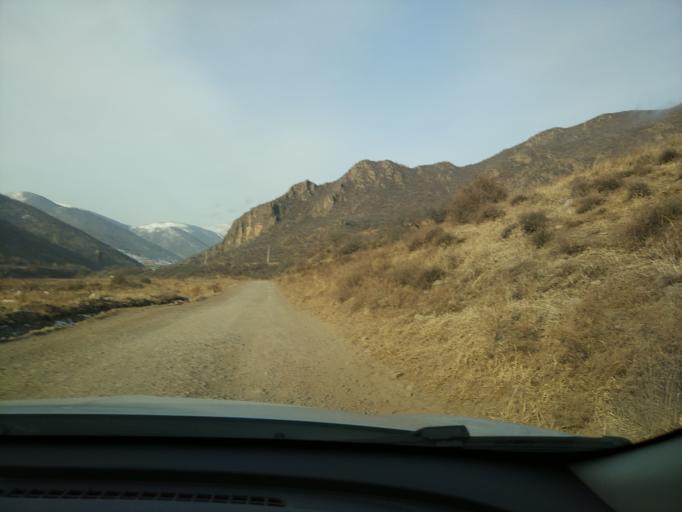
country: CN
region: Hebei
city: Xiwanzi
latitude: 40.8502
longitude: 115.4895
